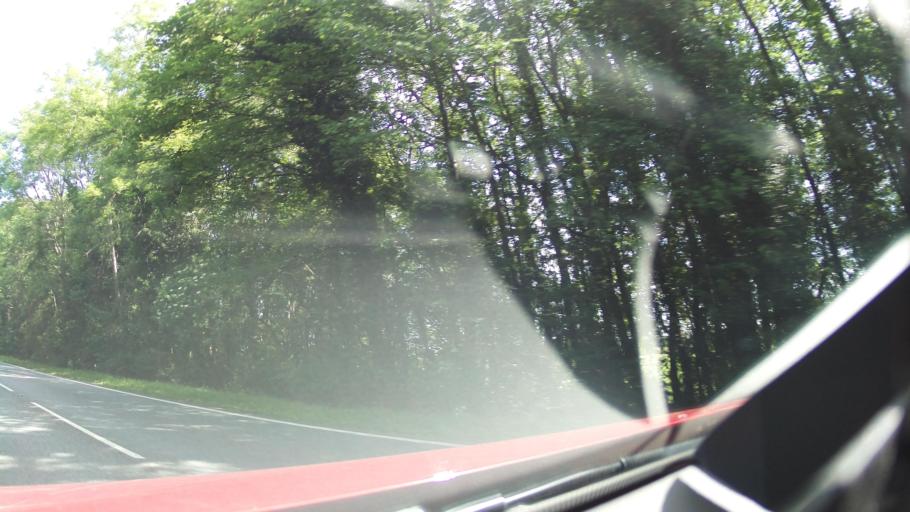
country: GB
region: England
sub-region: Lincolnshire
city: Burton
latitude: 53.2596
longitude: -0.5387
